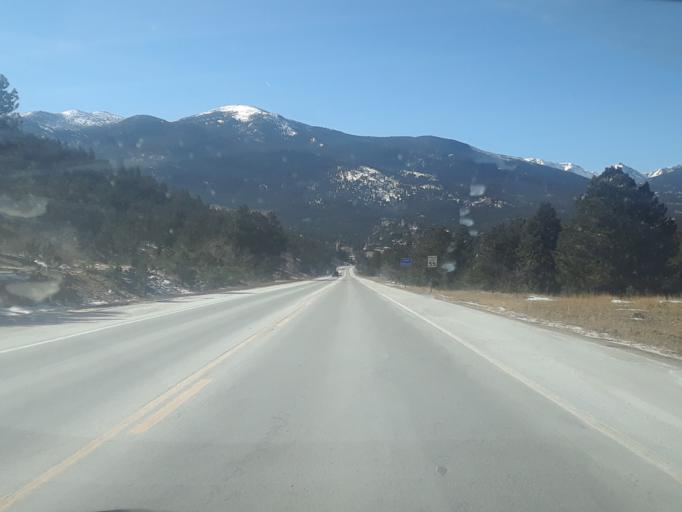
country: US
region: Colorado
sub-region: Larimer County
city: Estes Park
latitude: 40.1889
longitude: -105.4953
